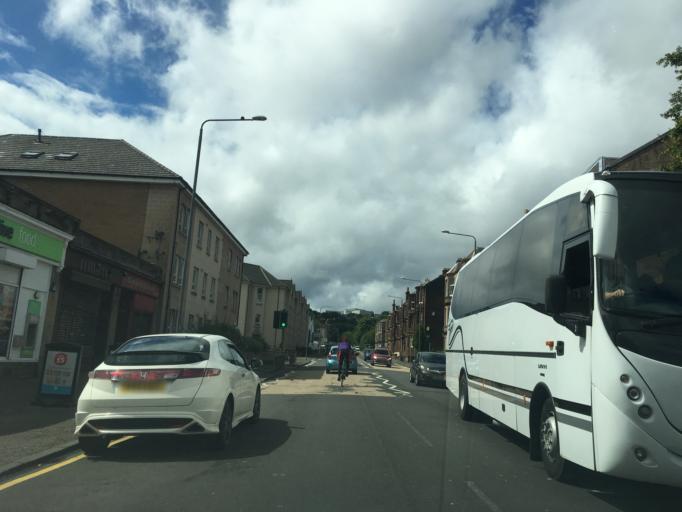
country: GB
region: Scotland
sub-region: Inverclyde
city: Gourock
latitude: 55.9562
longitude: -4.8049
